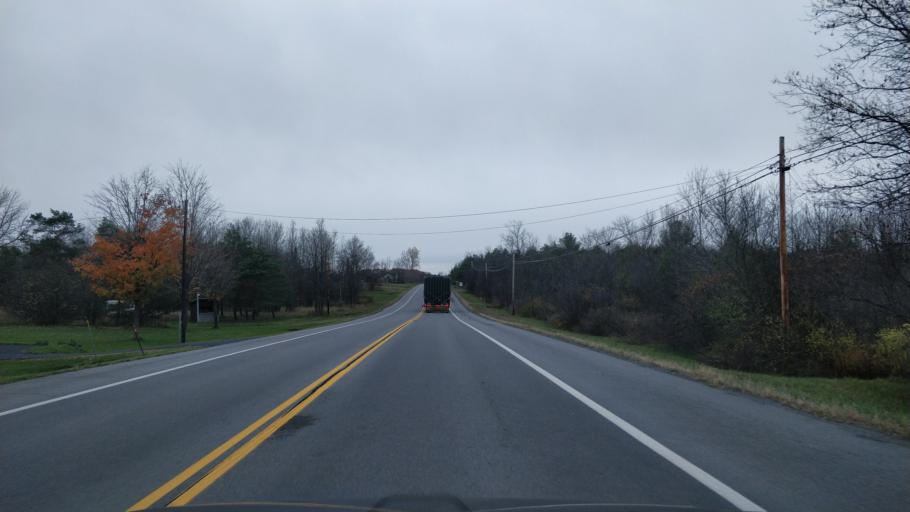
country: CA
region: Ontario
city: Brockville
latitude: 44.6215
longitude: -75.5924
